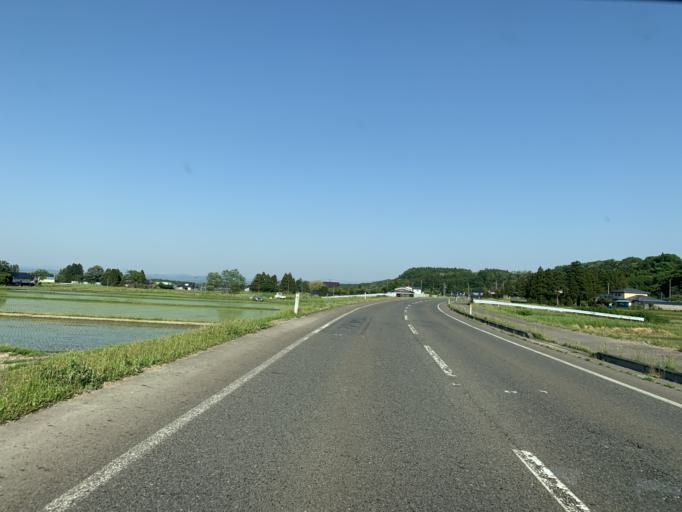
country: JP
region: Iwate
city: Kitakami
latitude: 39.2841
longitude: 141.0162
